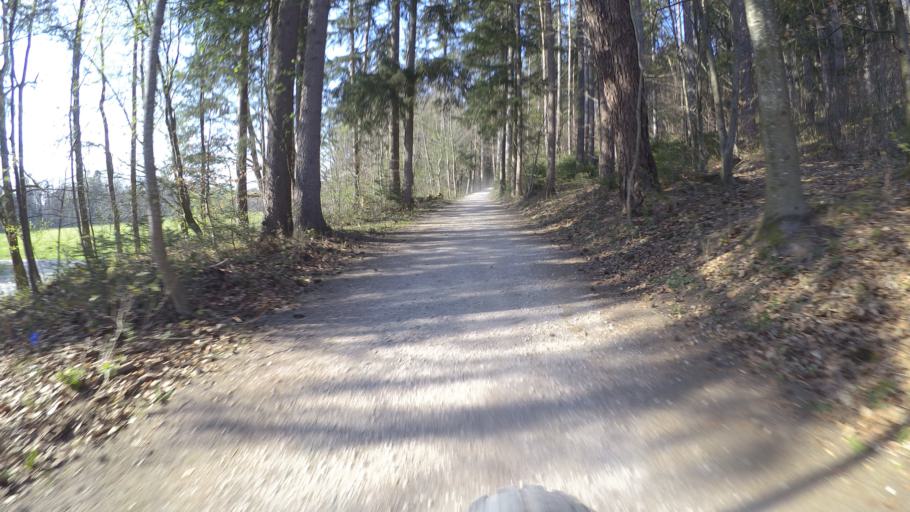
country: DE
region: Bavaria
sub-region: Upper Bavaria
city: Traunreut
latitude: 47.9529
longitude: 12.5886
